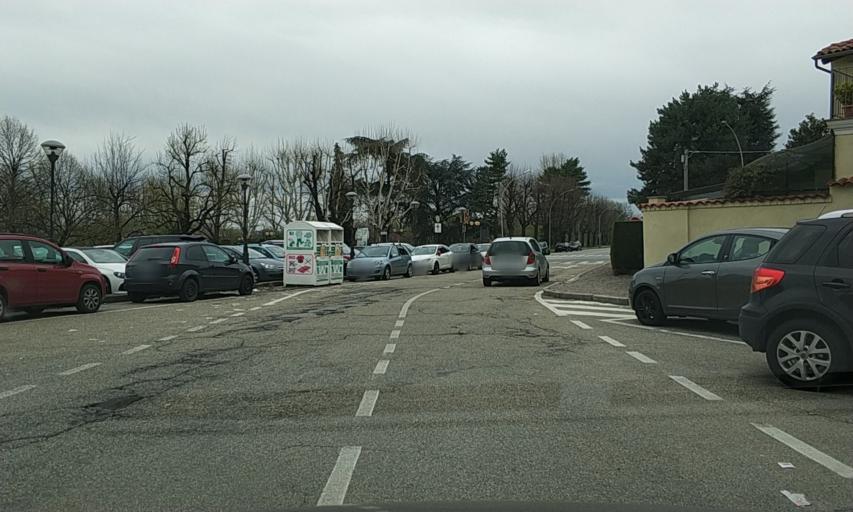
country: IT
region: Piedmont
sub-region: Provincia di Torino
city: Rivarolo Canavese
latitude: 45.3339
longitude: 7.7264
